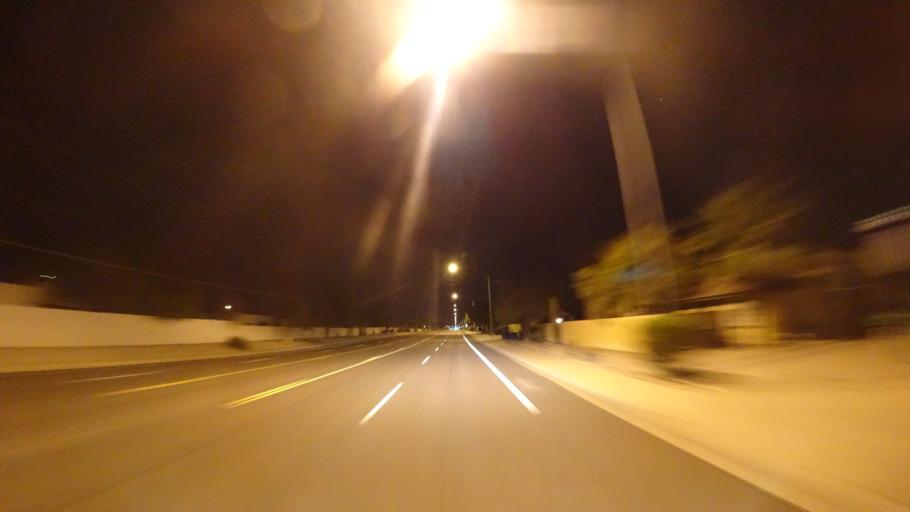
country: US
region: Arizona
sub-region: Maricopa County
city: Mesa
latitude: 33.4649
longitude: -111.7013
